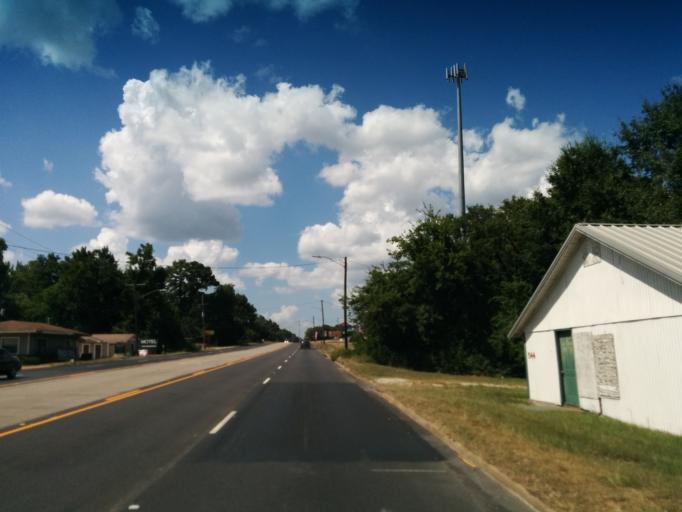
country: US
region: Texas
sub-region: Jasper County
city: Jasper
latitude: 30.9258
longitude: -93.9968
